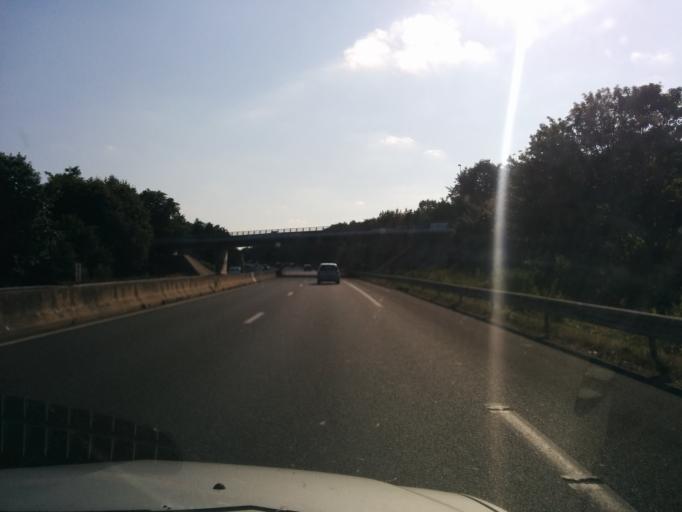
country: FR
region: Pays de la Loire
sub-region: Departement de la Loire-Atlantique
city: Carquefou
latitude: 47.2911
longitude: -1.4974
